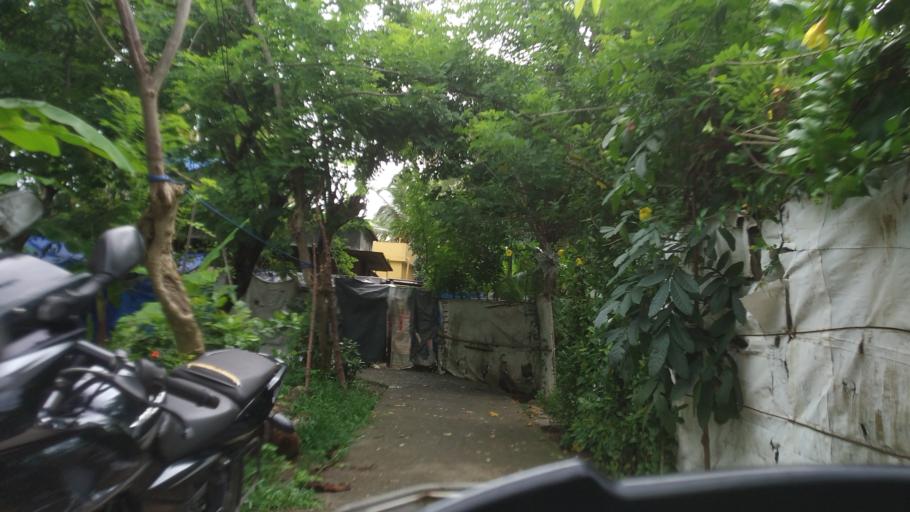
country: IN
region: Kerala
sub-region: Ernakulam
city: Elur
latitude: 10.0809
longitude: 76.2213
